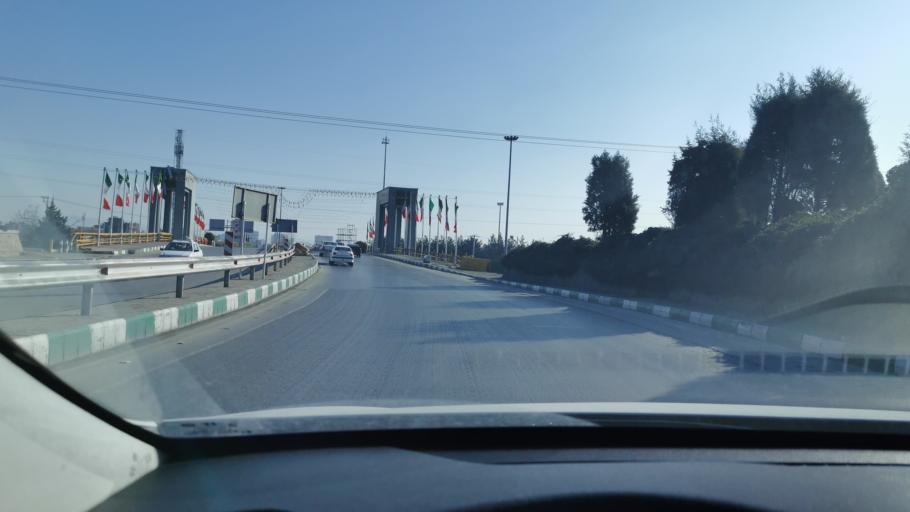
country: IR
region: Razavi Khorasan
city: Mashhad
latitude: 36.2624
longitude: 59.5822
